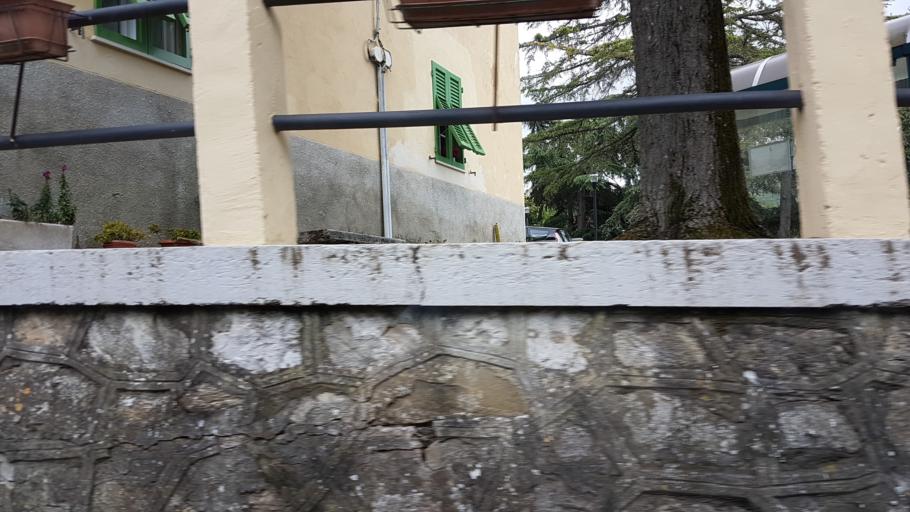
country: IT
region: Tuscany
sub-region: Province of Pisa
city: Santa Luce
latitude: 43.4728
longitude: 10.5651
